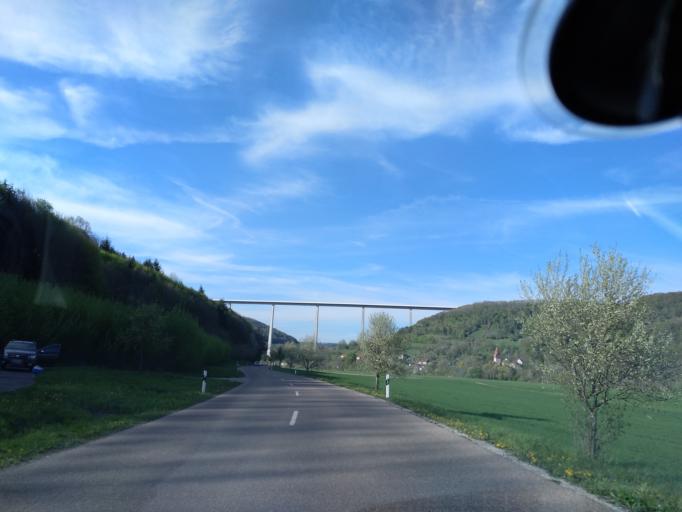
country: DE
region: Baden-Wuerttemberg
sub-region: Regierungsbezirk Stuttgart
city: Braunsbach
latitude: 49.1633
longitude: 9.7832
